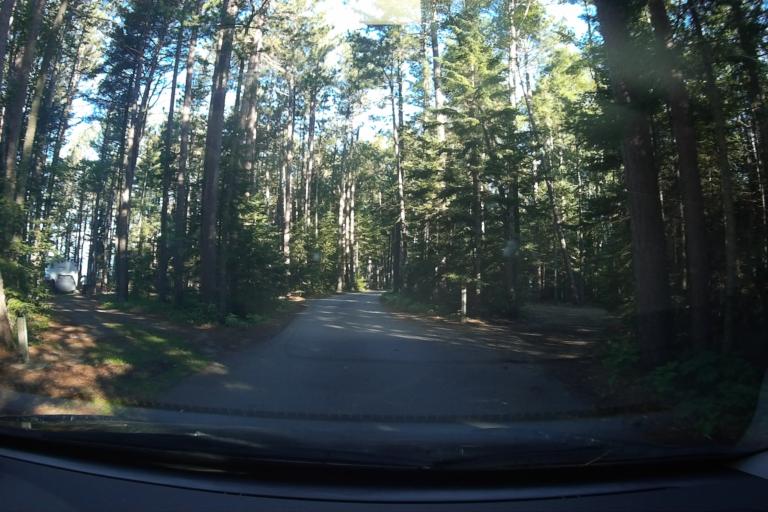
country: CA
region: Ontario
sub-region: Algoma
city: Sault Ste. Marie
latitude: 47.3307
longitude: -84.6134
